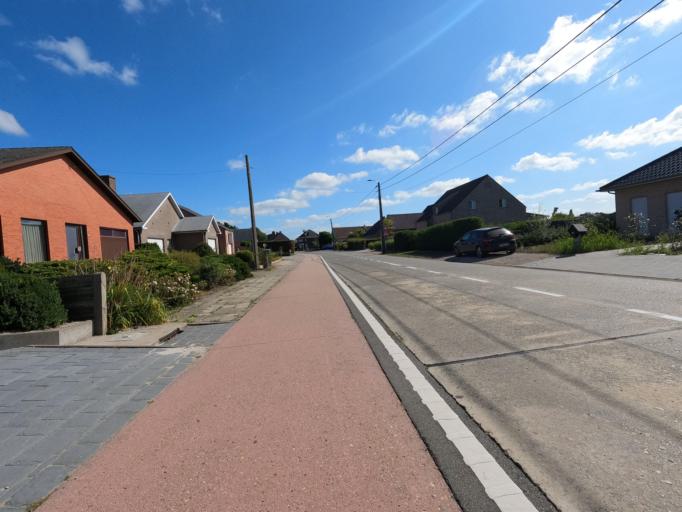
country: BE
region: Flanders
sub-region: Provincie Antwerpen
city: Hulshout
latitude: 51.1028
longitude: 4.7842
